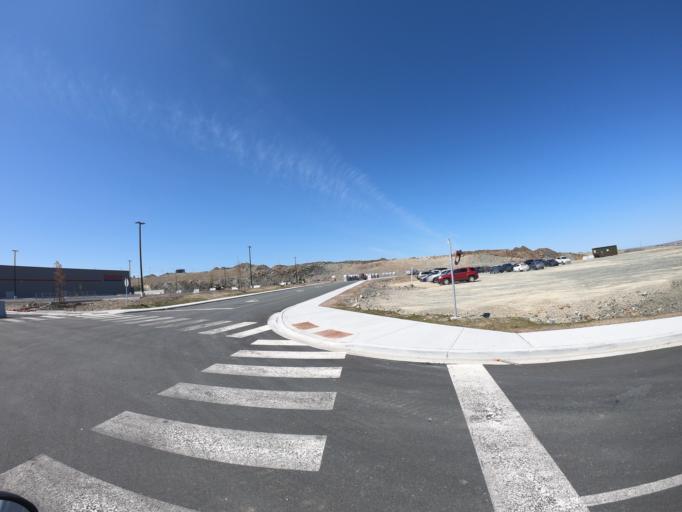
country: CA
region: Newfoundland and Labrador
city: Mount Pearl
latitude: 47.5080
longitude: -52.8358
